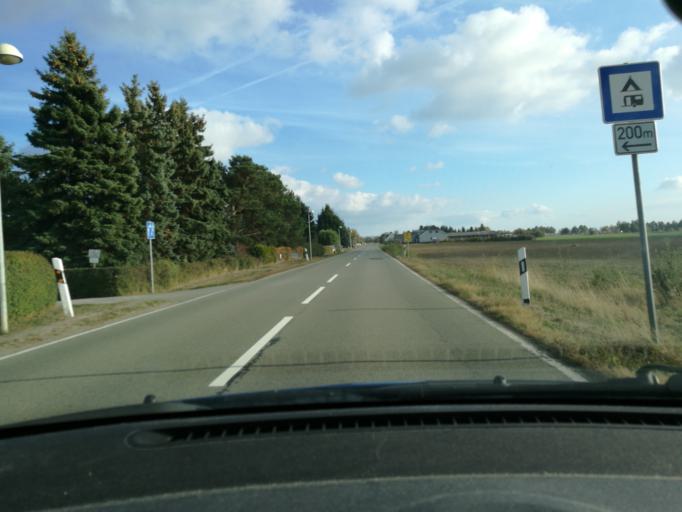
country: DE
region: Saxony-Anhalt
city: Luftkurort Arendsee
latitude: 52.8783
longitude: 11.4590
